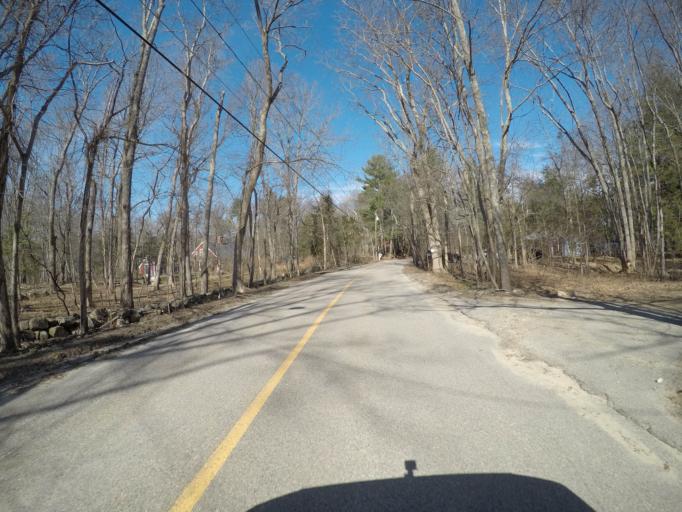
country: US
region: Massachusetts
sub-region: Norfolk County
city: Sharon
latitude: 42.0929
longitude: -71.1565
